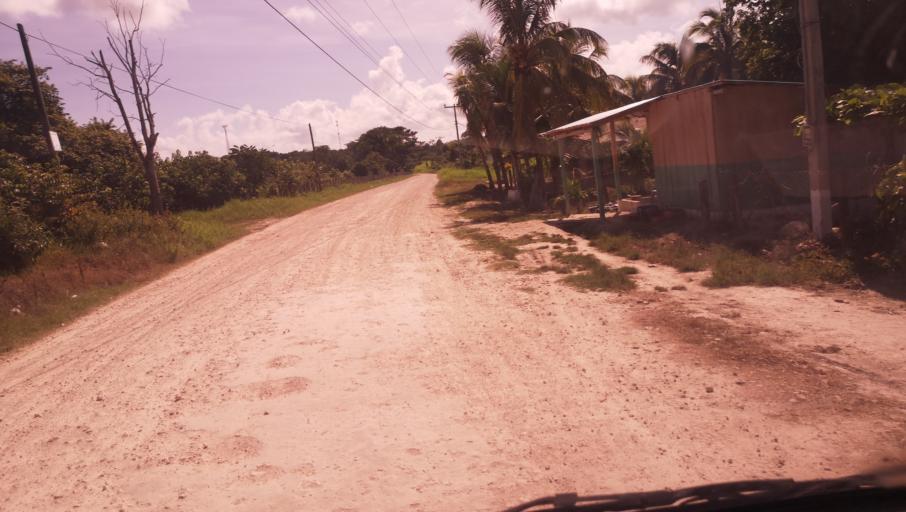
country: GT
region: Peten
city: Dolores
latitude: 16.7895
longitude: -89.3061
